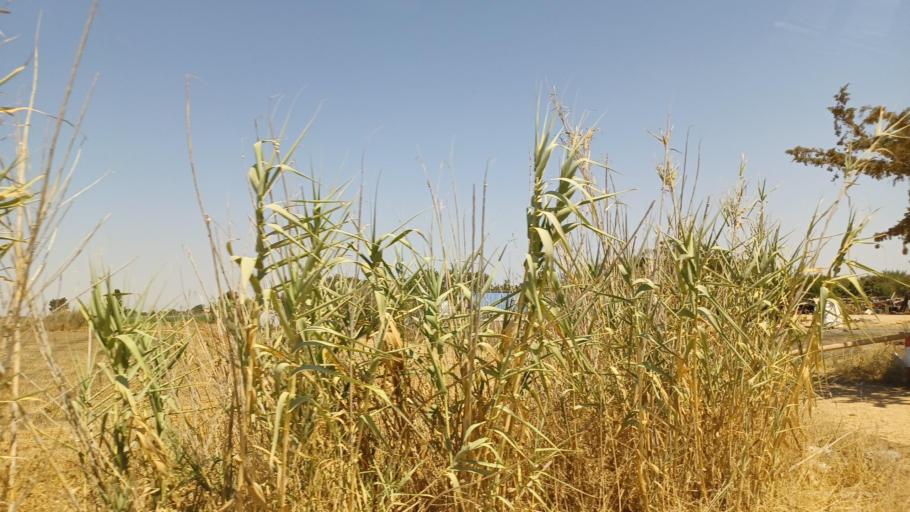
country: CY
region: Ammochostos
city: Avgorou
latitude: 35.0239
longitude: 33.8209
